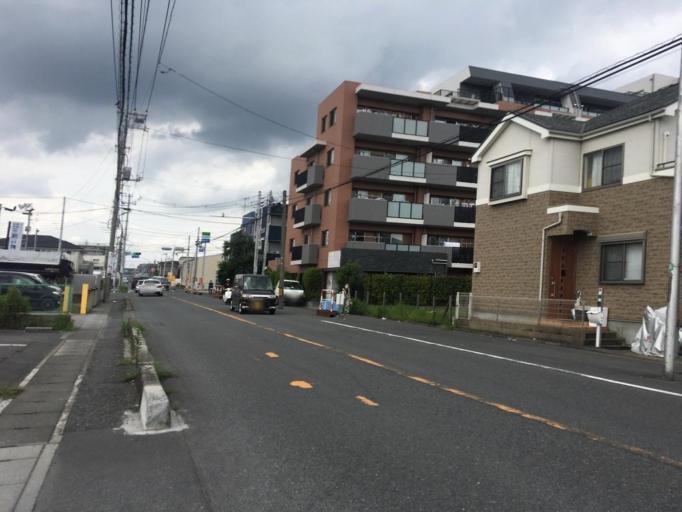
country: JP
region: Saitama
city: Shimotoda
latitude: 35.8178
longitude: 139.6615
